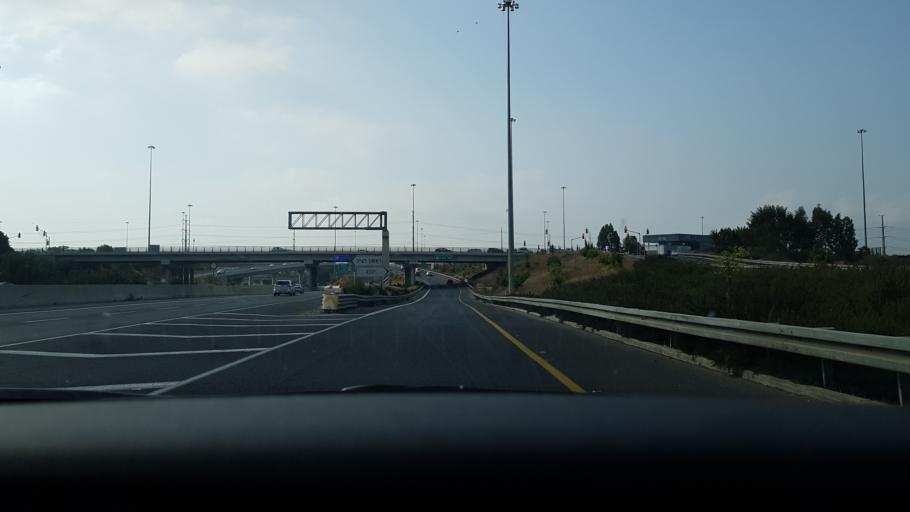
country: IL
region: Central District
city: Rishon LeZiyyon
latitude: 31.9580
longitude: 34.7852
